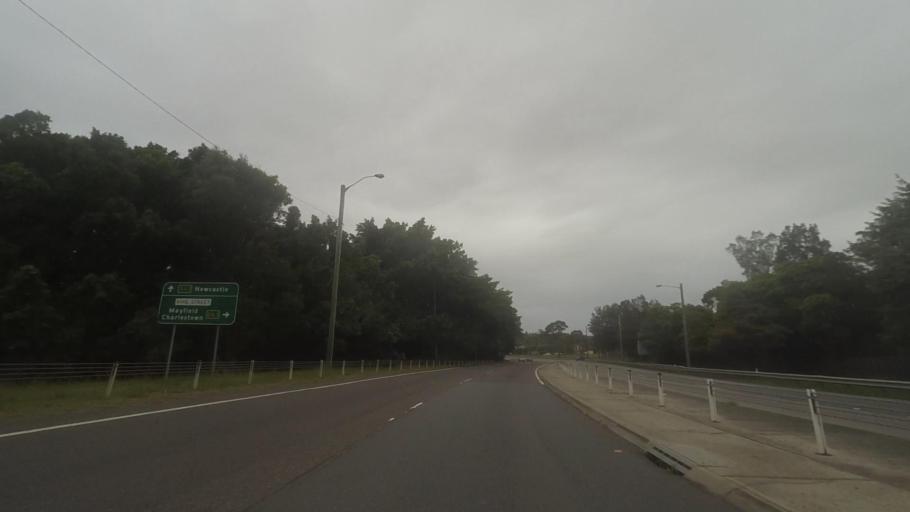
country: AU
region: New South Wales
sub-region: Newcastle
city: Mayfield
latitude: -32.8888
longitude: 151.7391
